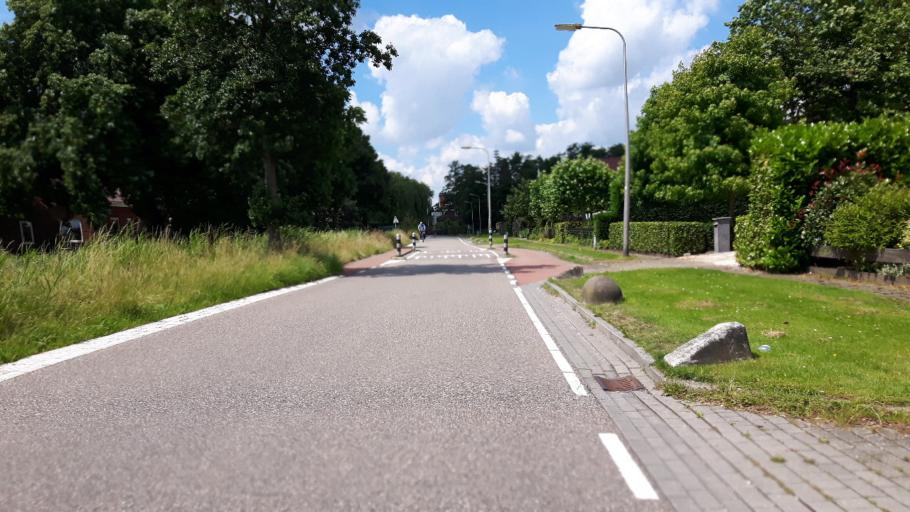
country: NL
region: South Holland
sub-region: Gemeente Waddinxveen
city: Oranjewijk
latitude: 52.0442
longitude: 4.6705
